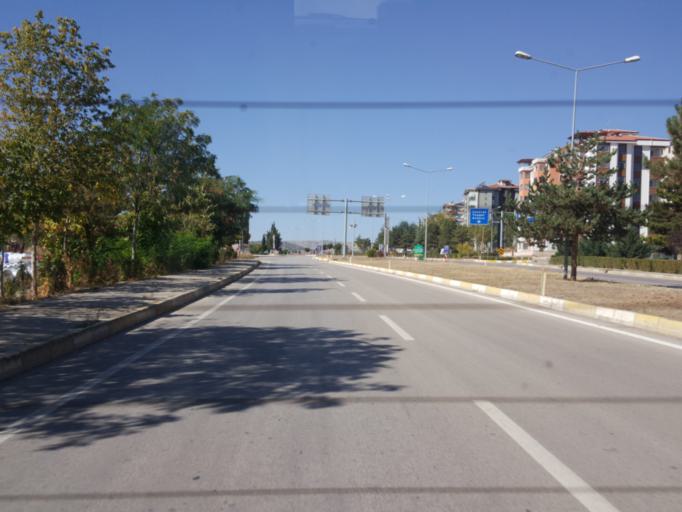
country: TR
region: Tokat
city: Zile
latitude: 40.2921
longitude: 35.8752
